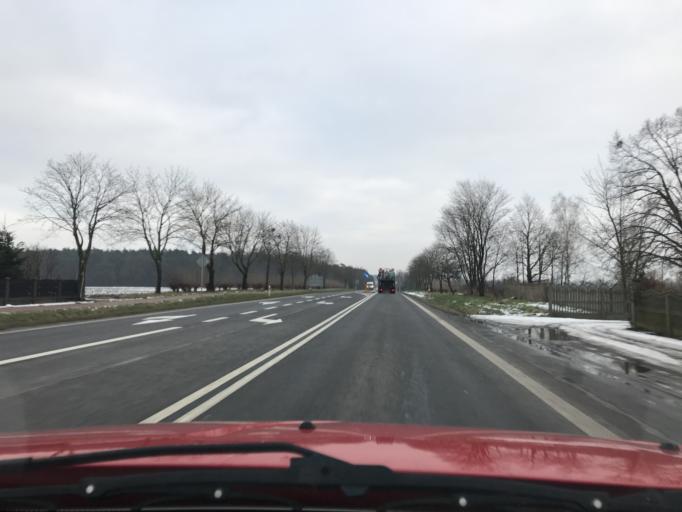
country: PL
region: Greater Poland Voivodeship
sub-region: Powiat pleszewski
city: Goluchow
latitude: 51.8642
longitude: 17.9037
